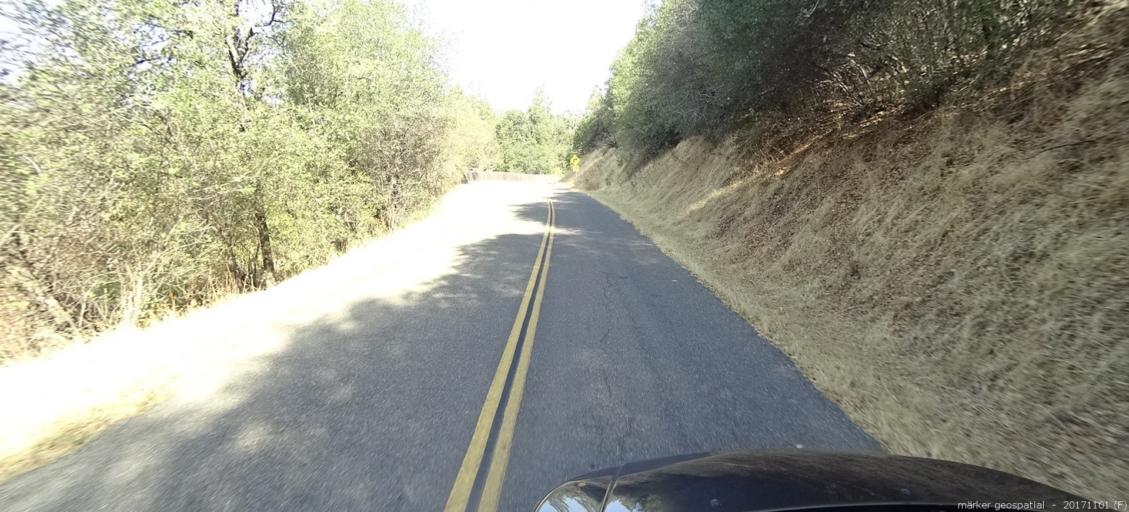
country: US
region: California
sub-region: Shasta County
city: Shasta Lake
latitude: 40.7147
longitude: -122.3287
